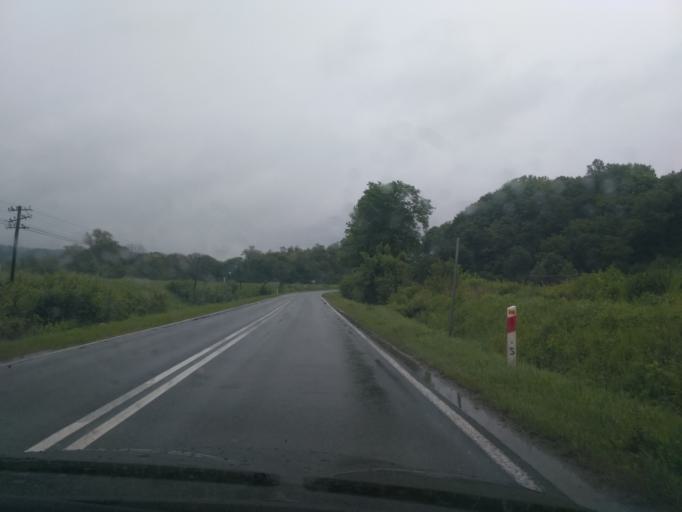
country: PL
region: Subcarpathian Voivodeship
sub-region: Powiat strzyzowski
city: Frysztak
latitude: 49.8201
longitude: 21.6305
